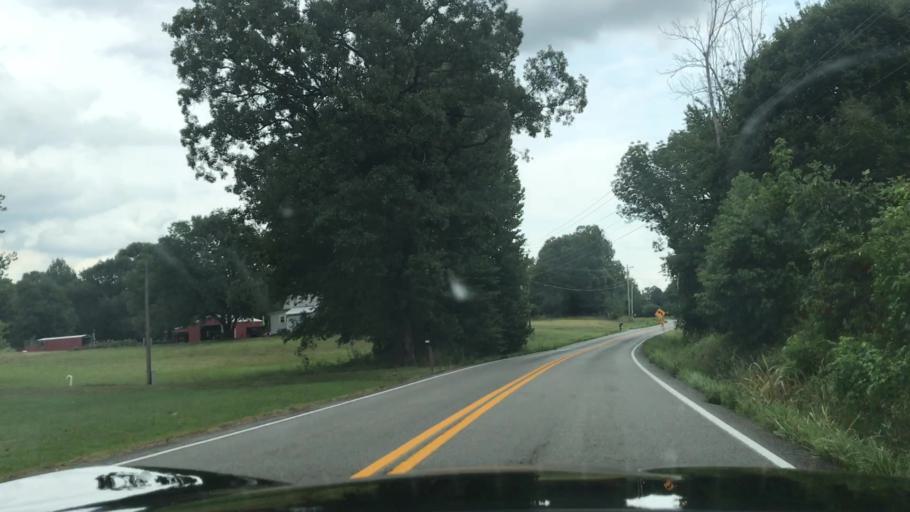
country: US
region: Kentucky
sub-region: Muhlenberg County
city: Central City
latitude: 37.2046
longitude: -86.9406
